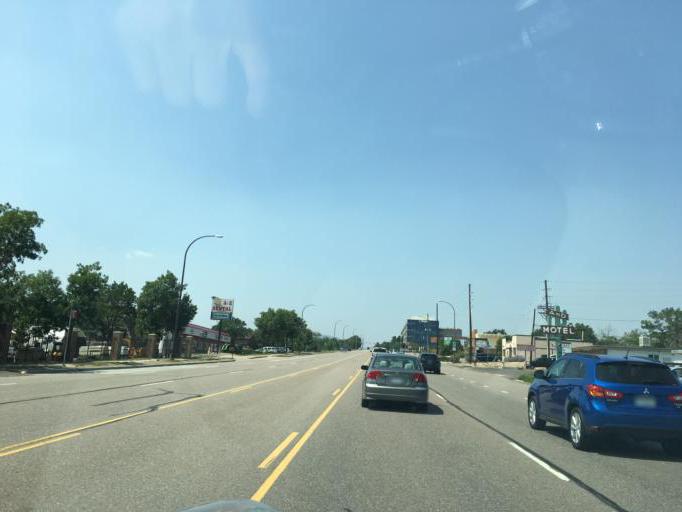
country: US
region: Colorado
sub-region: Jefferson County
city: Applewood
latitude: 39.7402
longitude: -105.1306
